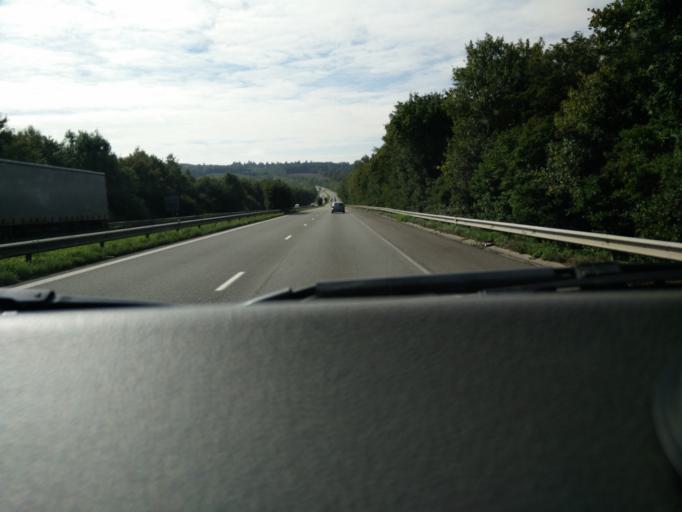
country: BE
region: Wallonia
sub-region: Province de Namur
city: Ciney
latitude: 50.2460
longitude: 5.0497
